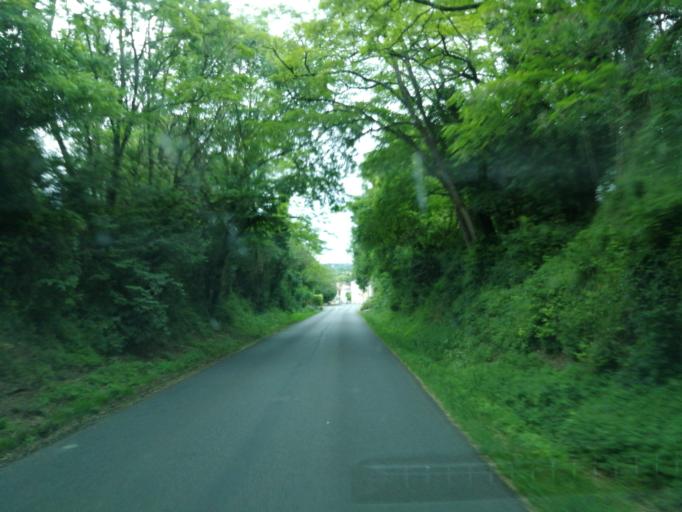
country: FR
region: Pays de la Loire
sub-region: Departement de la Vendee
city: Vix
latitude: 46.3720
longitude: -0.9165
